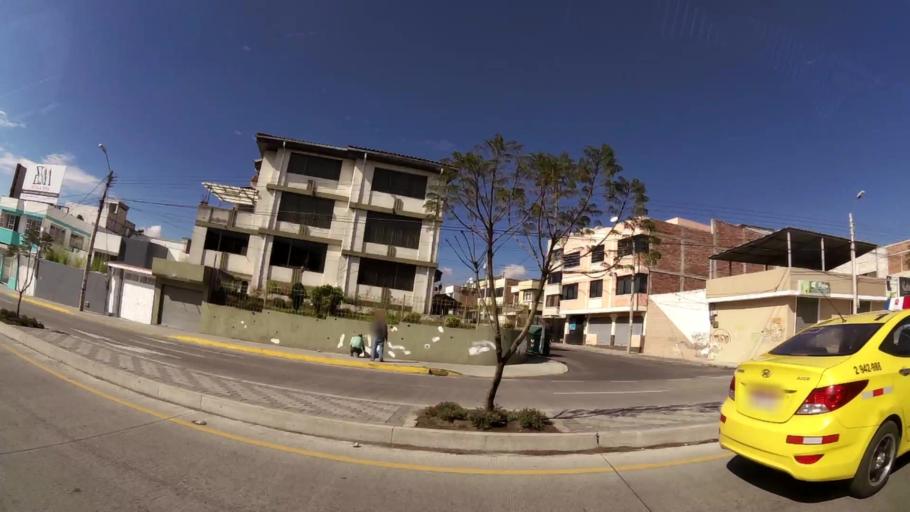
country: EC
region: Chimborazo
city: Riobamba
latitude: -1.6566
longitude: -78.6643
